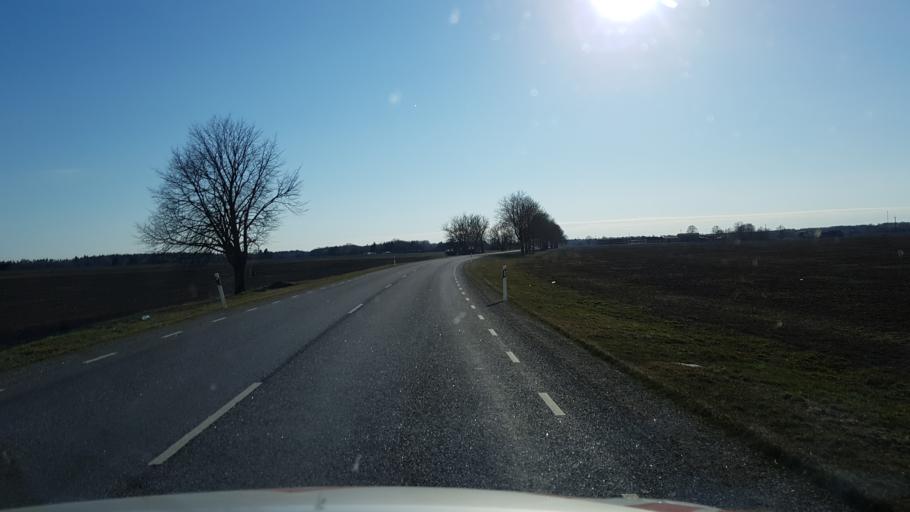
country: EE
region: Ida-Virumaa
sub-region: Johvi vald
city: Johvi
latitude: 59.3395
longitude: 27.3496
